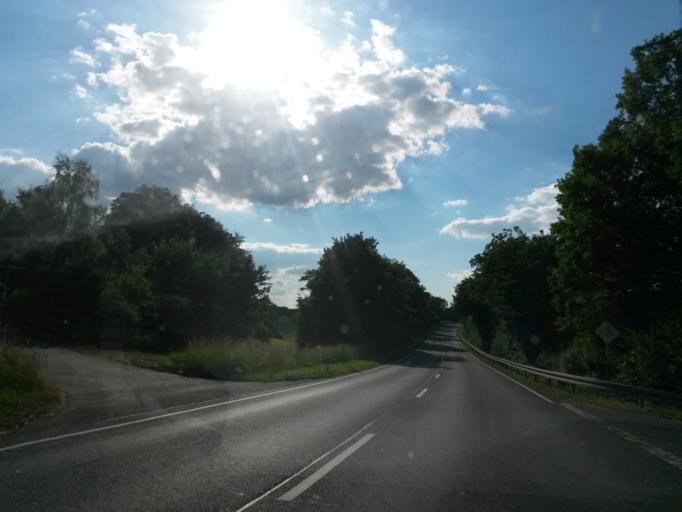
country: DE
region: Bavaria
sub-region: Regierungsbezirk Mittelfranken
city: Hagenbuchach
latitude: 49.5219
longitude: 10.7520
